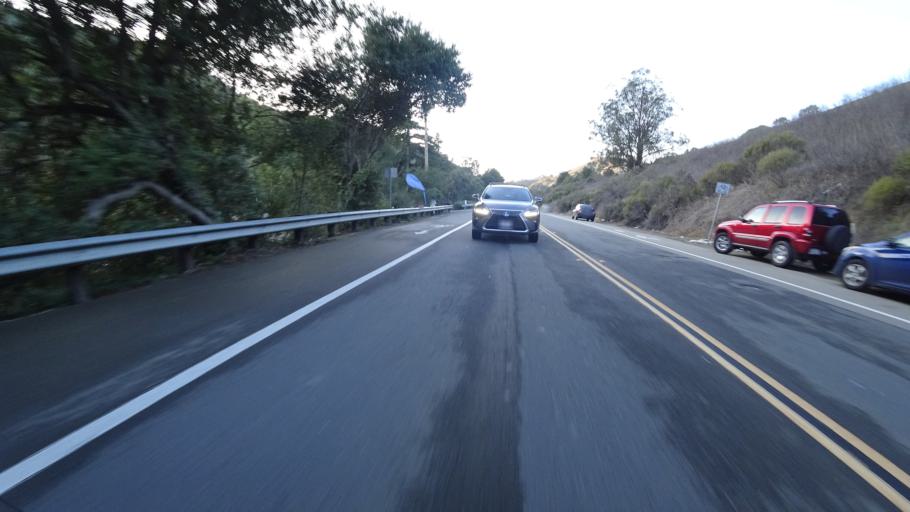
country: US
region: California
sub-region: Alameda County
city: Fairview
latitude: 37.6994
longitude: -122.0305
